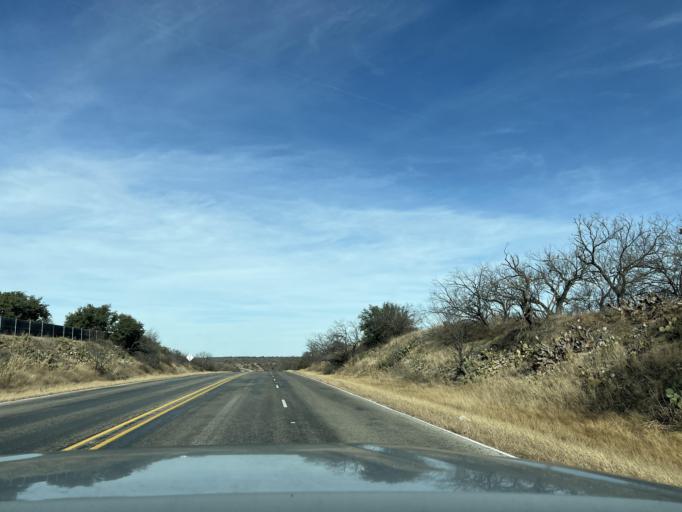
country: US
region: Texas
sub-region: Eastland County
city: Cisco
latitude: 32.4291
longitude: -98.9852
